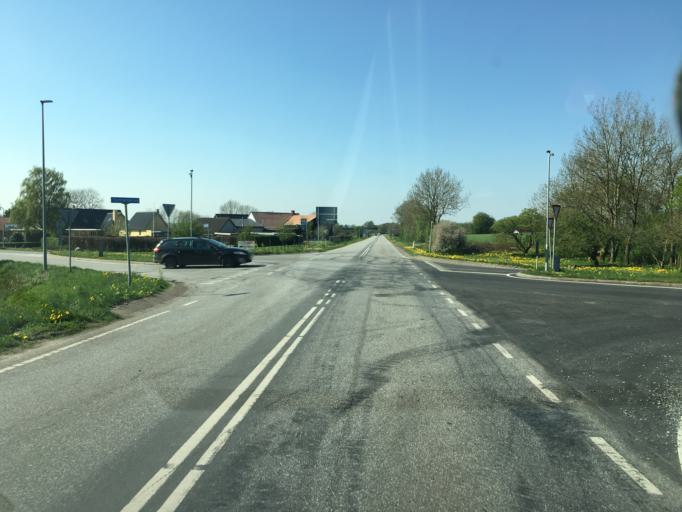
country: DK
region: South Denmark
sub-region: Haderslev Kommune
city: Vojens
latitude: 55.3211
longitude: 9.3129
